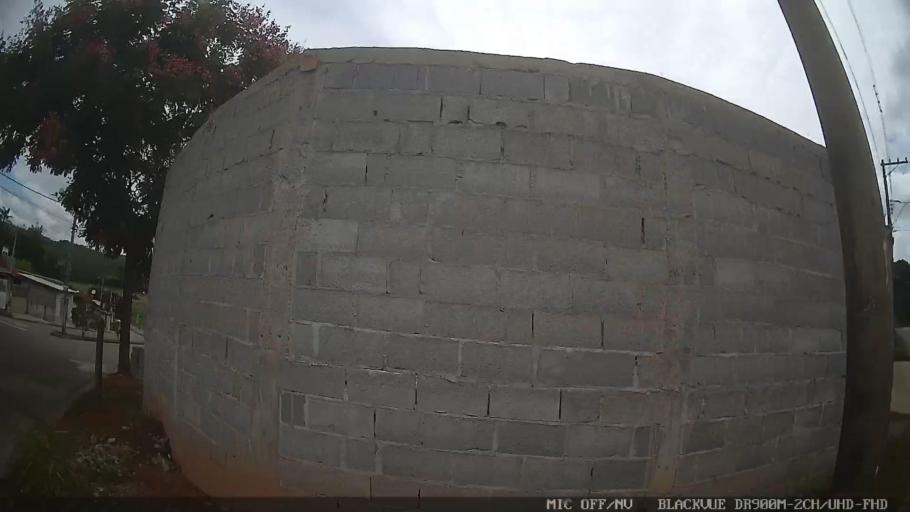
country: BR
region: Minas Gerais
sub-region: Extrema
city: Extrema
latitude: -22.7437
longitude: -46.3749
